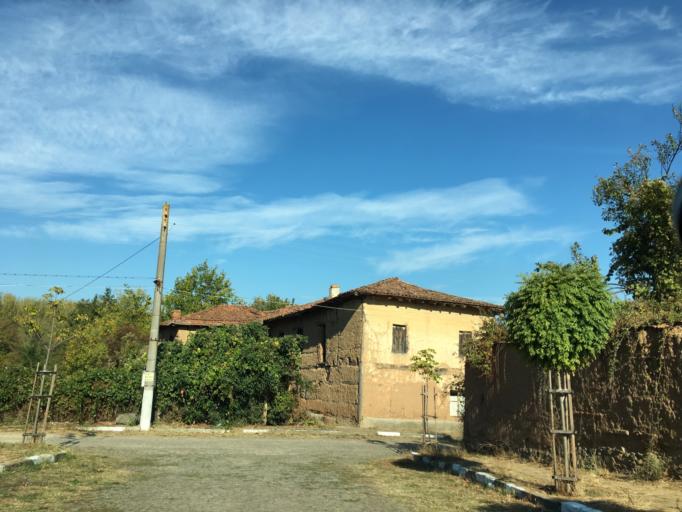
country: BG
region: Khaskovo
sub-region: Obshtina Ivaylovgrad
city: Ivaylovgrad
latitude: 41.3918
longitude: 26.1318
